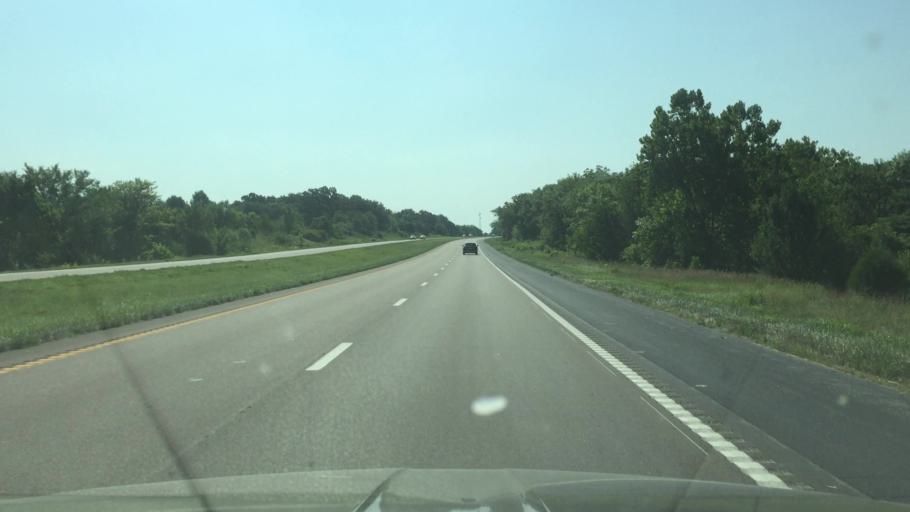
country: US
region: Missouri
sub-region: Pettis County
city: La Monte
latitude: 38.7422
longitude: -93.3270
